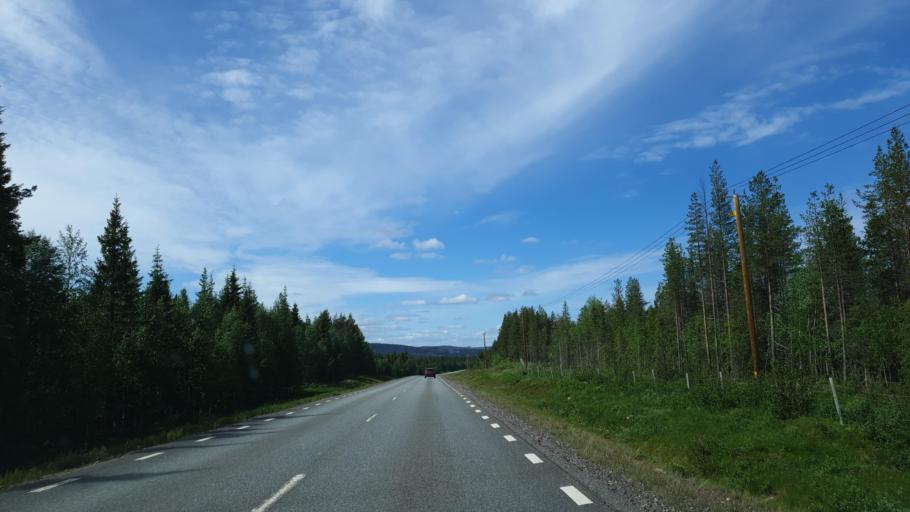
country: SE
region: Norrbotten
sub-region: Arvidsjaurs Kommun
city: Arvidsjaur
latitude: 65.6109
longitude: 18.7534
